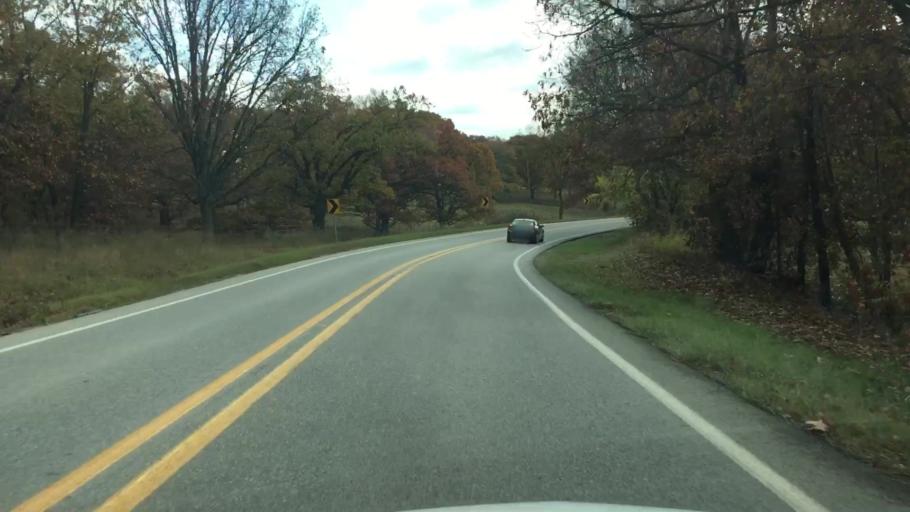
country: US
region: Arkansas
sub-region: Benton County
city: Gentry
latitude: 36.2619
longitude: -94.4506
